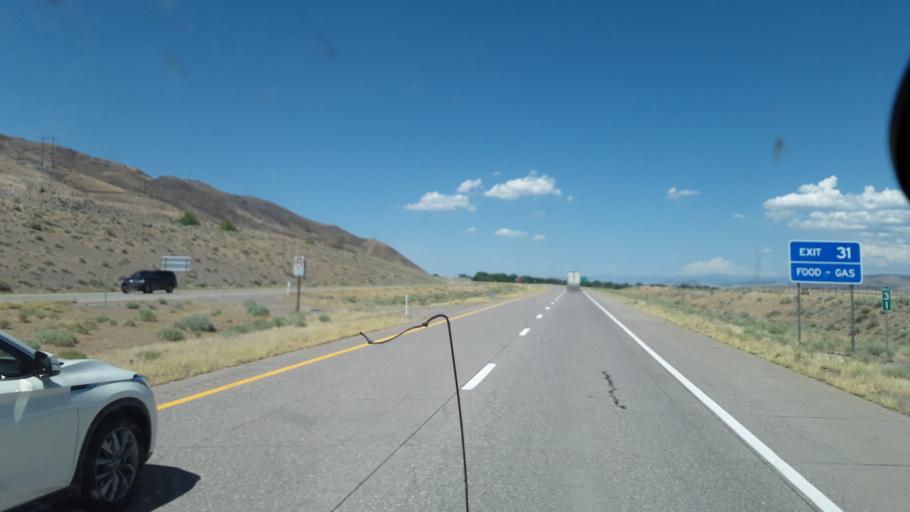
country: US
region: Utah
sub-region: Sevier County
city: Monroe
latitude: 38.6721
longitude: -112.1633
